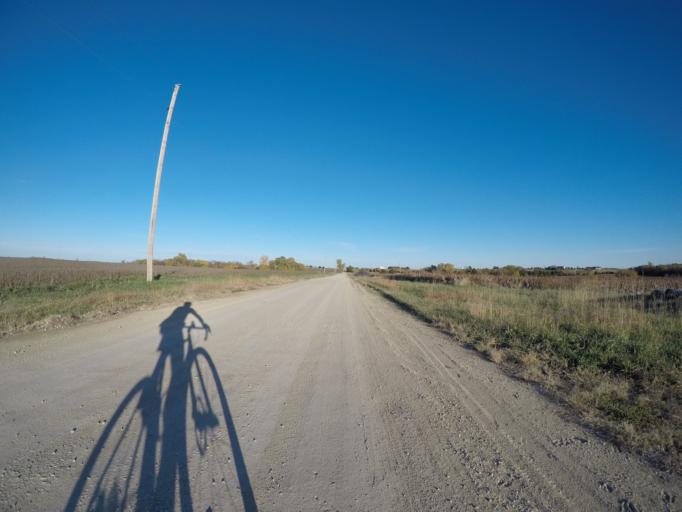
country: US
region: Kansas
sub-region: Riley County
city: Manhattan
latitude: 39.2691
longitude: -96.6947
